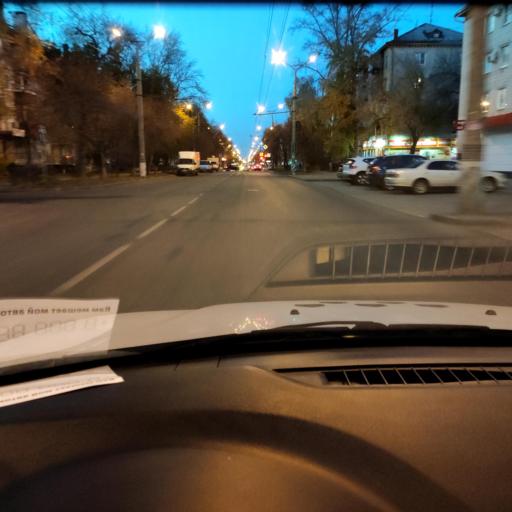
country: RU
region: Samara
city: Tol'yatti
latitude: 53.5146
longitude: 49.4172
